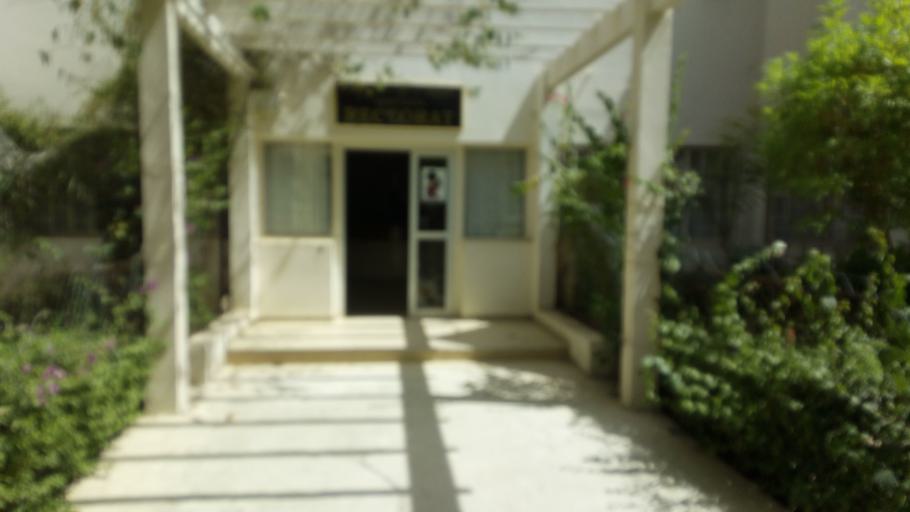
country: SN
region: Saint-Louis
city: Saint-Louis
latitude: 16.0625
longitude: -16.4212
